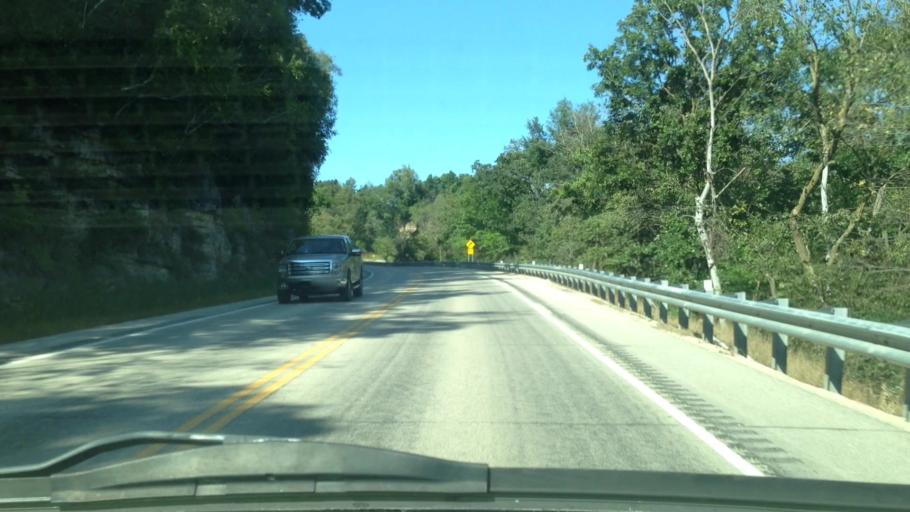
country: US
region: Minnesota
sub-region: Fillmore County
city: Rushford
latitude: 43.8425
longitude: -91.7540
